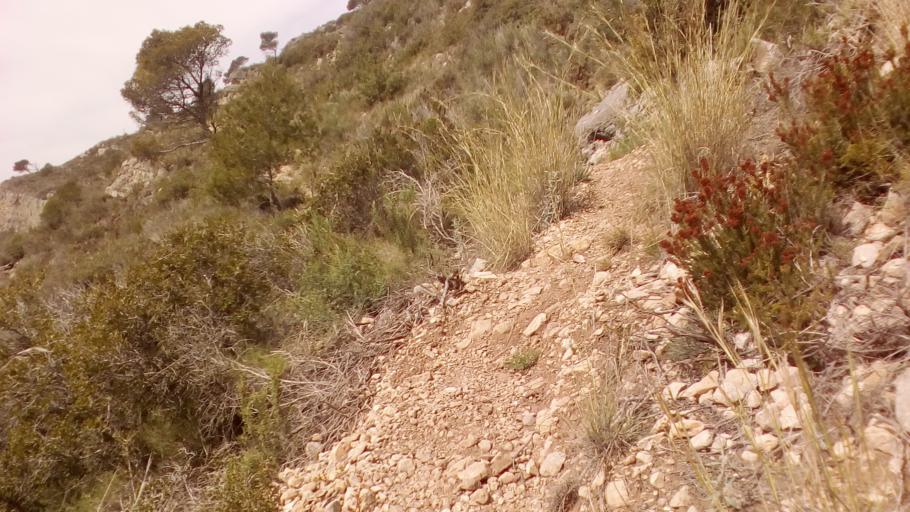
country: ES
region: Valencia
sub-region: Provincia de Valencia
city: Xeraco,Jaraco
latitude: 39.0388
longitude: -0.2394
